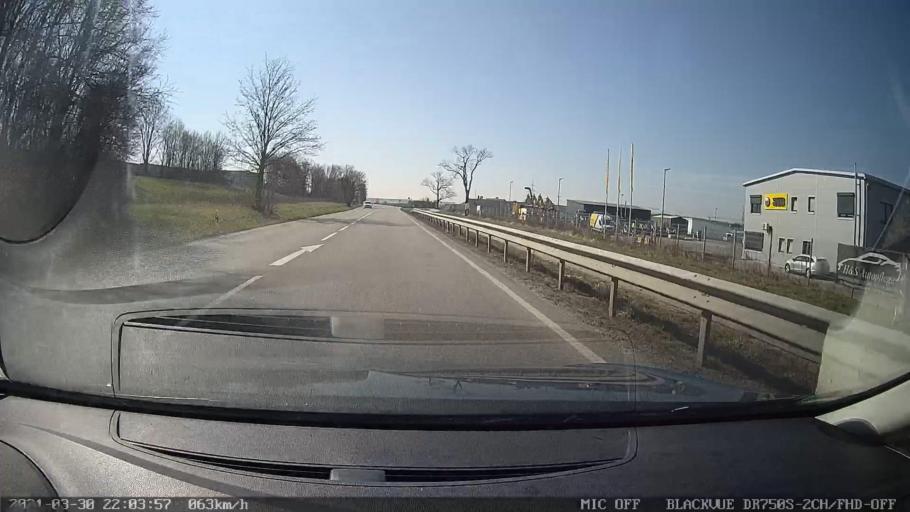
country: DE
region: Bavaria
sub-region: Upper Palatinate
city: Regenstauf
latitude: 49.1099
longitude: 12.1248
